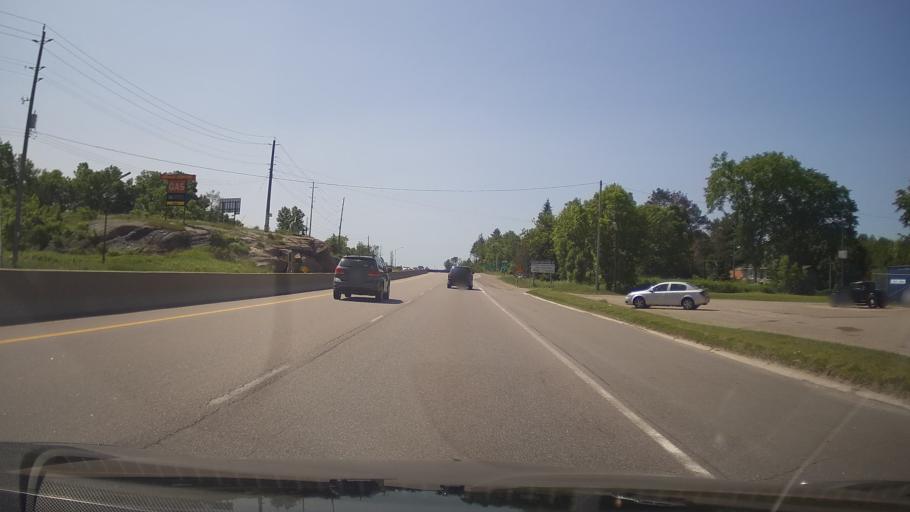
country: CA
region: Ontario
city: Gravenhurst
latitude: 44.7741
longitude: -79.3349
